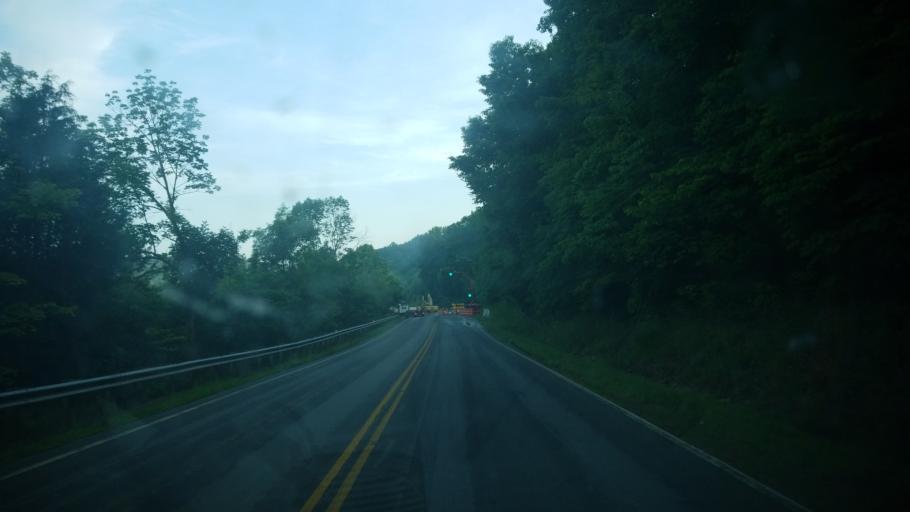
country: US
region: Ohio
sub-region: Adams County
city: Peebles
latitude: 38.8754
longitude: -83.4598
